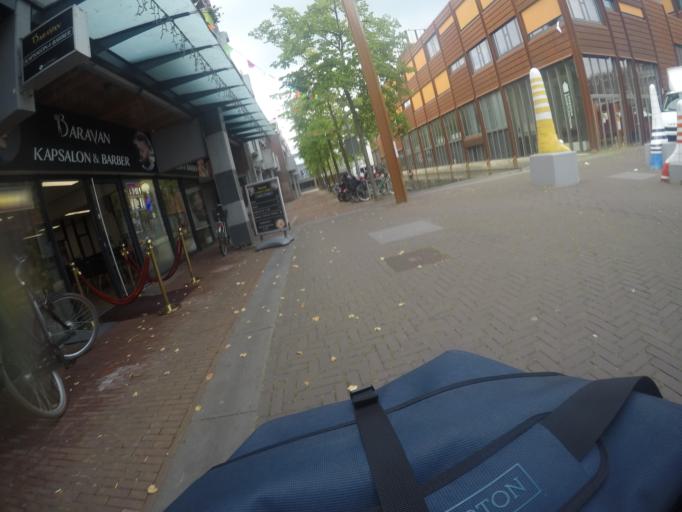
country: NL
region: Flevoland
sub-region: Gemeente Almere
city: Almere Stad
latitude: 52.3360
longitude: 5.2186
